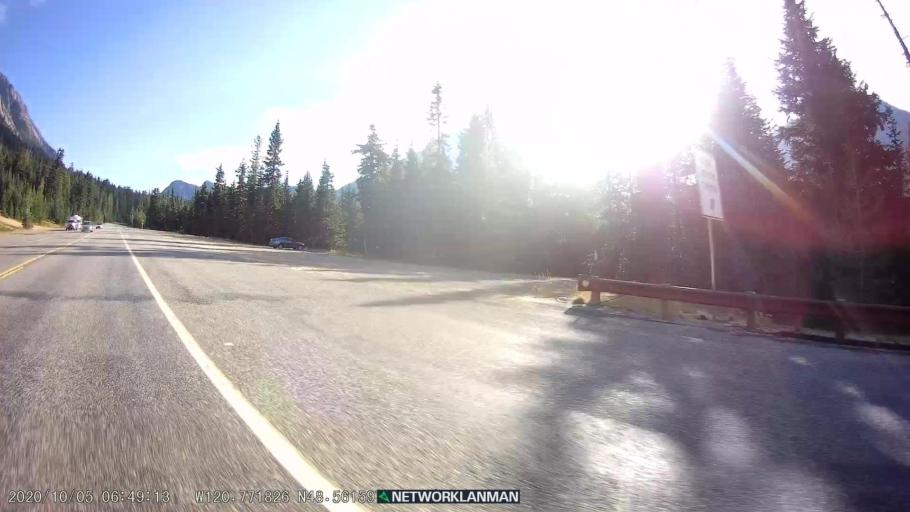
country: US
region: Washington
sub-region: Chelan County
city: Granite Falls
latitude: 48.5613
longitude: -120.7715
